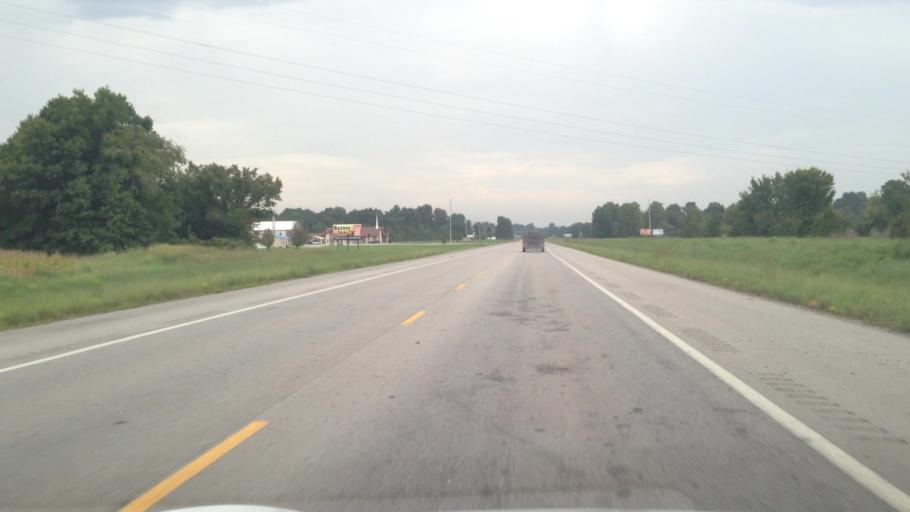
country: US
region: Kansas
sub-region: Cherokee County
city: Baxter Springs
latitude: 37.0705
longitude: -94.7220
